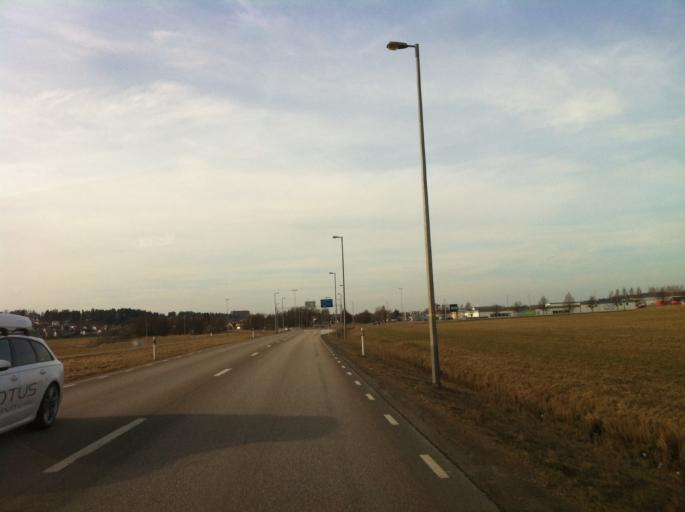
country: SE
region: Vaermland
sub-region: Kristinehamns Kommun
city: Kristinehamn
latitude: 59.2933
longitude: 14.1275
